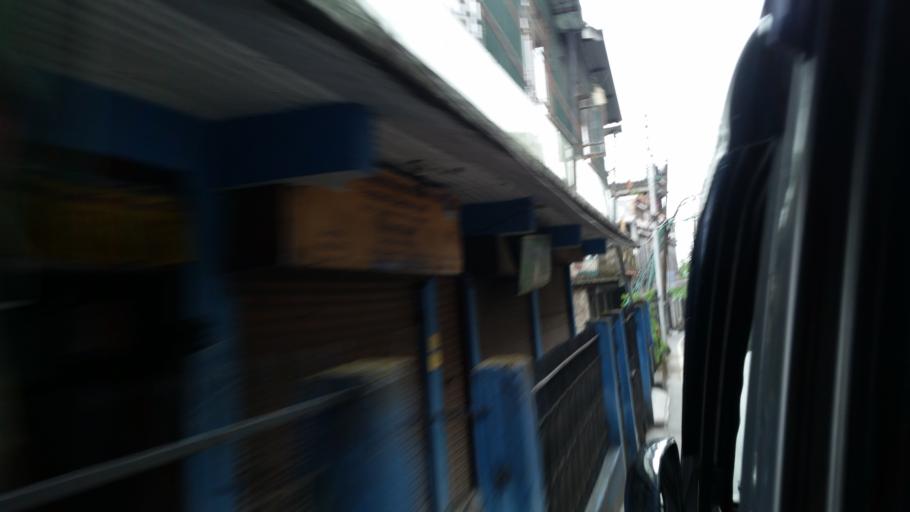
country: IN
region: West Bengal
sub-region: Darjiling
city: Darjiling
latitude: 27.0316
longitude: 88.2570
